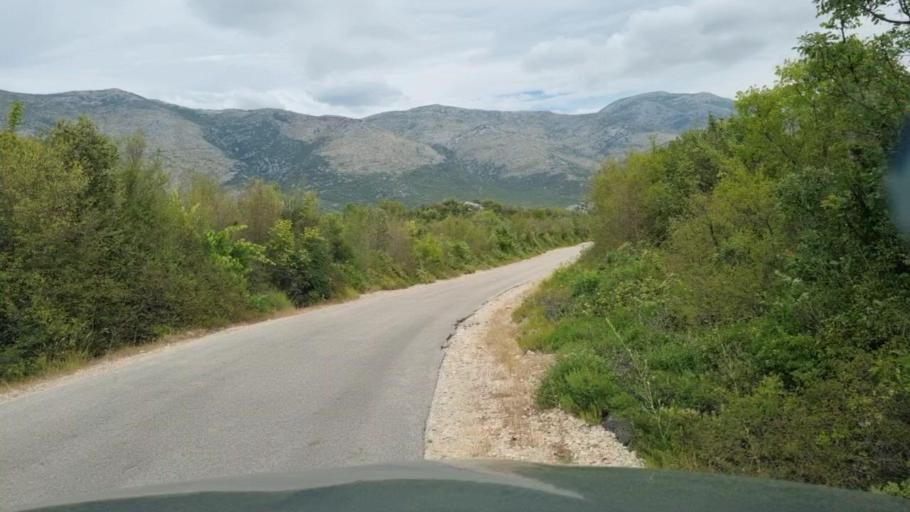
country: BA
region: Federation of Bosnia and Herzegovina
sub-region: Hercegovacko-Bosanski Kanton
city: Neum
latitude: 42.9480
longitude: 17.7029
